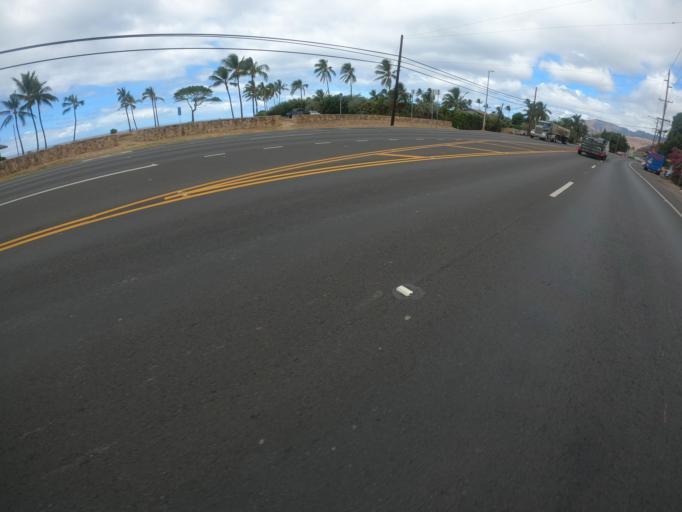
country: US
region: Hawaii
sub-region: Honolulu County
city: Ma'ili
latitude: 21.4058
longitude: -158.1771
